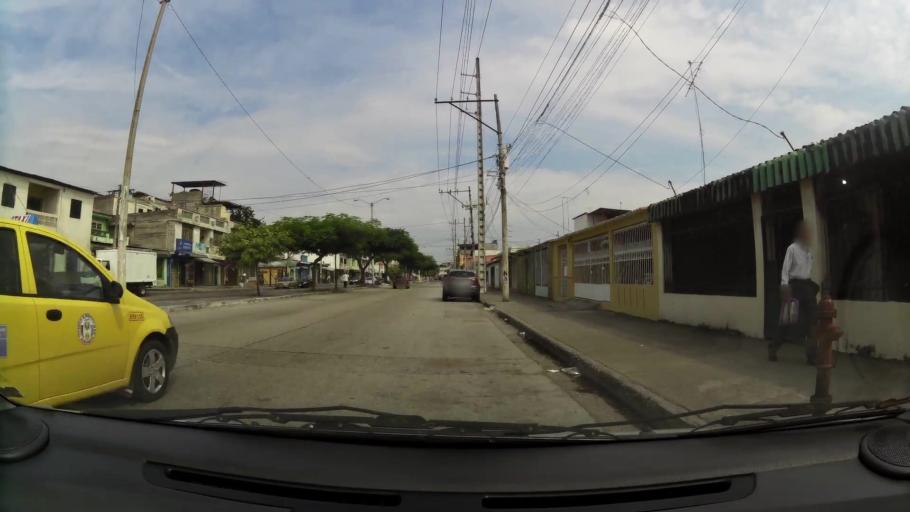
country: EC
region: Guayas
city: Guayaquil
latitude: -2.2483
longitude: -79.8996
